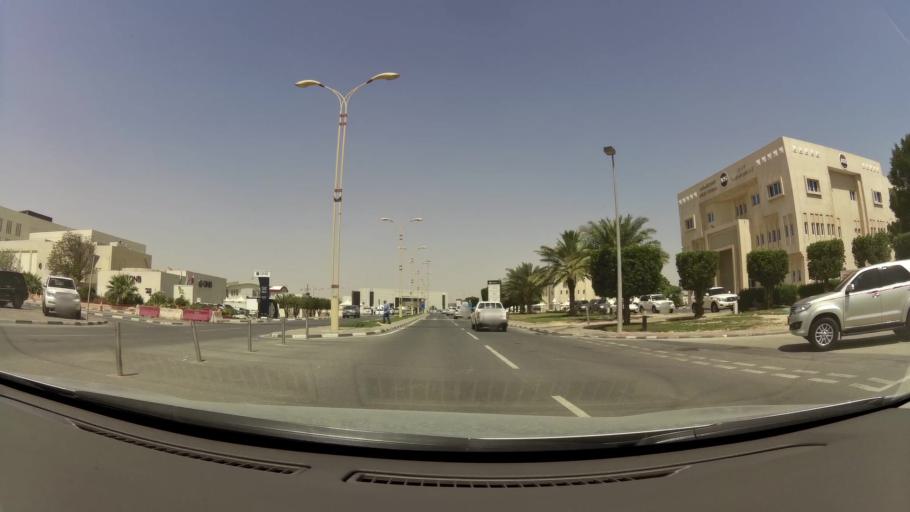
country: QA
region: Baladiyat Umm Salal
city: Umm Salal Muhammad
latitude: 25.3770
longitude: 51.4919
